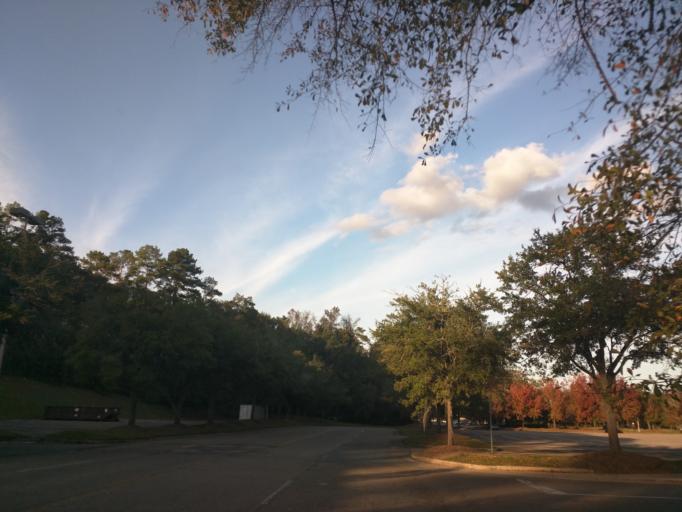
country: US
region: Florida
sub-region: Leon County
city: Tallahassee
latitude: 30.4370
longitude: -84.2570
